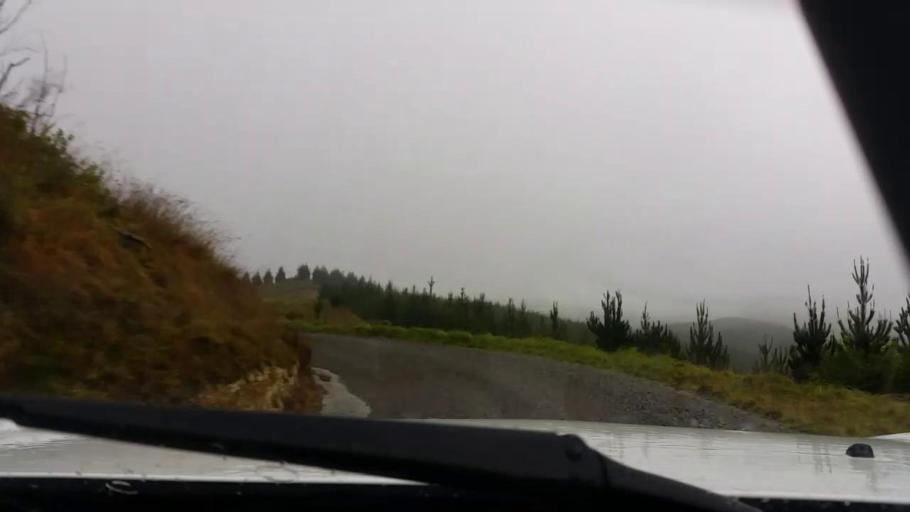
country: NZ
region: Wellington
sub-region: Masterton District
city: Masterton
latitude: -41.1925
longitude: 175.8119
